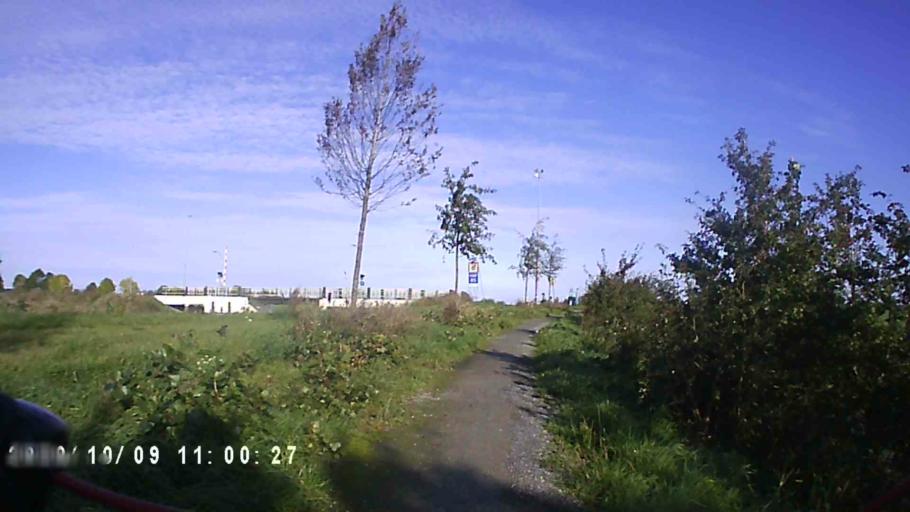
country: NL
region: Groningen
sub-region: Gemeente Zuidhorn
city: Aduard
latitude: 53.2578
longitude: 6.5095
